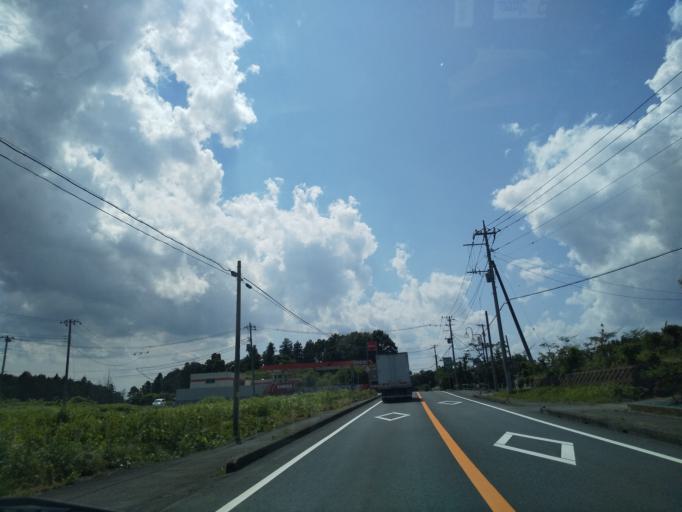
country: JP
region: Ibaraki
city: Ishioka
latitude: 36.1613
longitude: 140.3788
